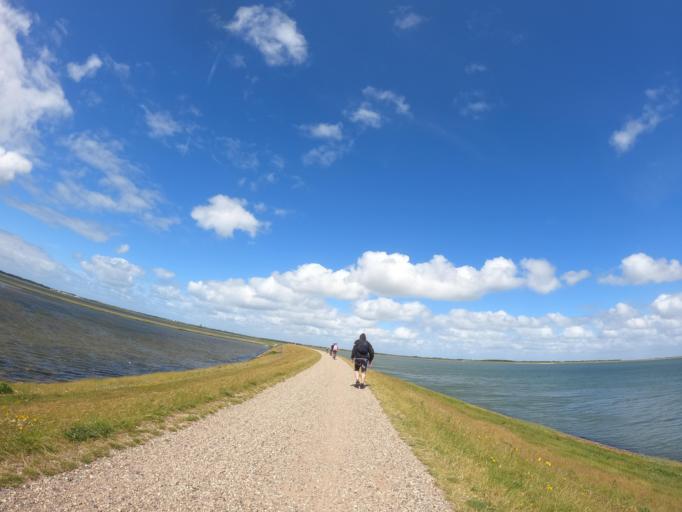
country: DE
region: Schleswig-Holstein
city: Tinnum
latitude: 54.8660
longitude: 8.3335
